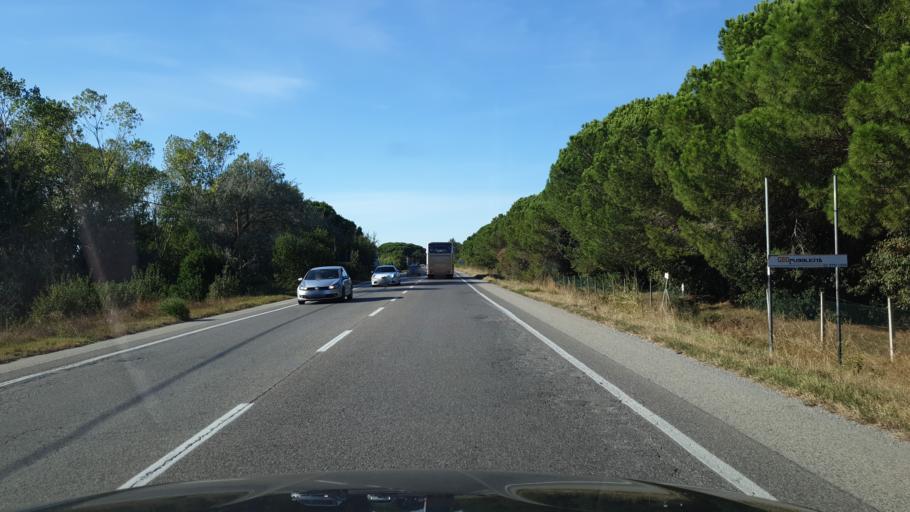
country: IT
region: Emilia-Romagna
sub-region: Provincia di Ravenna
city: Cervia
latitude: 44.2760
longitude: 12.3220
